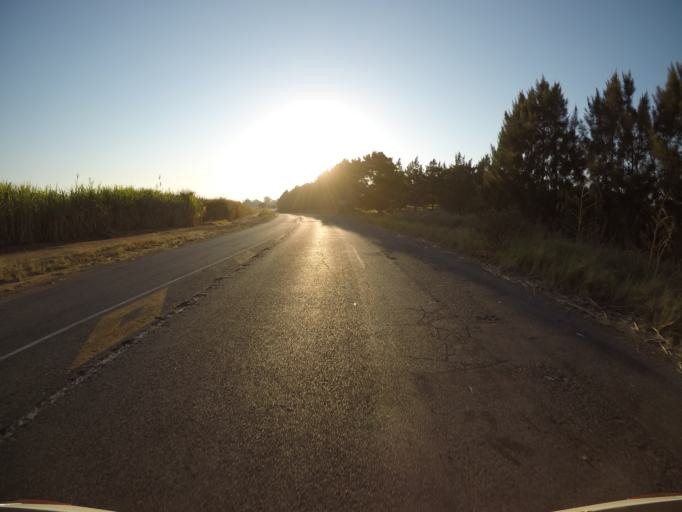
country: ZA
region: KwaZulu-Natal
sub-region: uThungulu District Municipality
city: Eshowe
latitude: -28.9485
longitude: 31.6775
